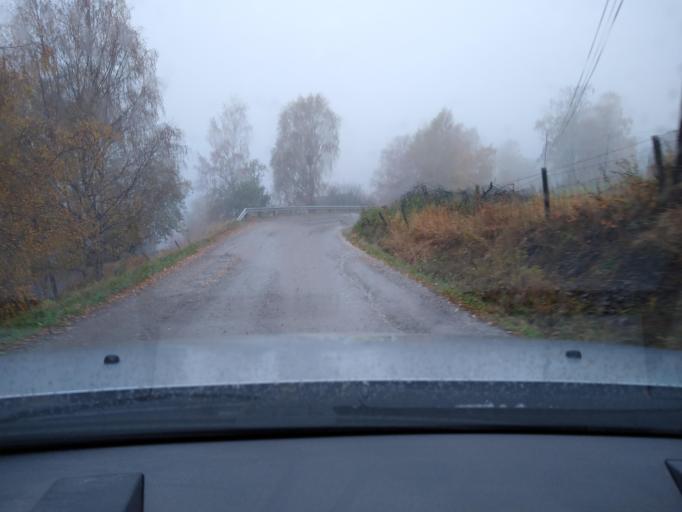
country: NO
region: Oppland
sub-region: Ringebu
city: Ringebu
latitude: 61.5294
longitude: 10.1552
